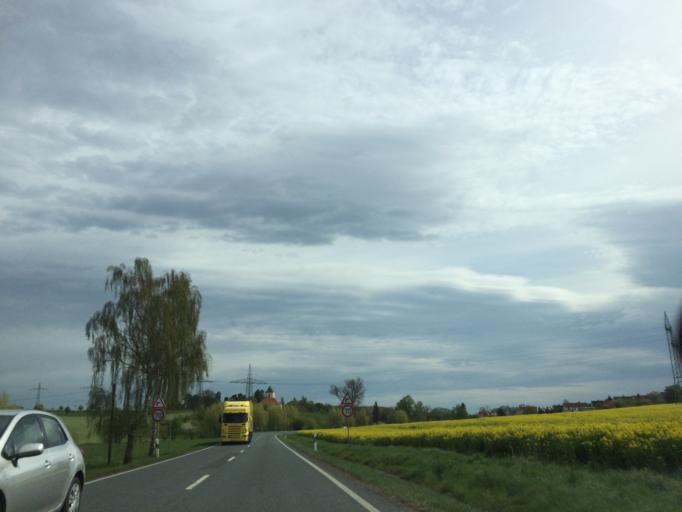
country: DE
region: Thuringia
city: Krolpa
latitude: 50.6746
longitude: 11.5266
